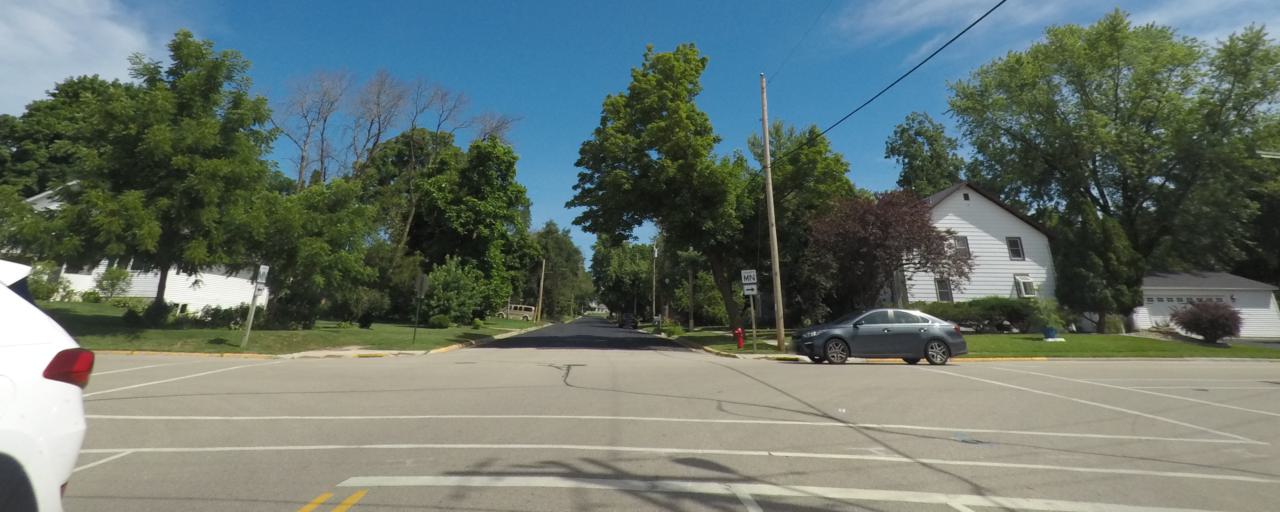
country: US
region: Wisconsin
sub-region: Dane County
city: McFarland
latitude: 43.0154
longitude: -89.2887
